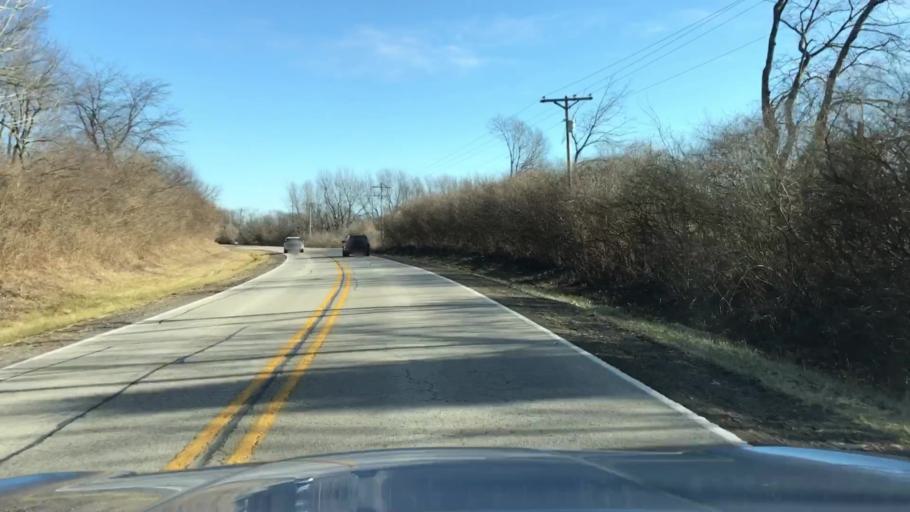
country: US
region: Illinois
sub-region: McLean County
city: Lexington
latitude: 40.6455
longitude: -88.8363
